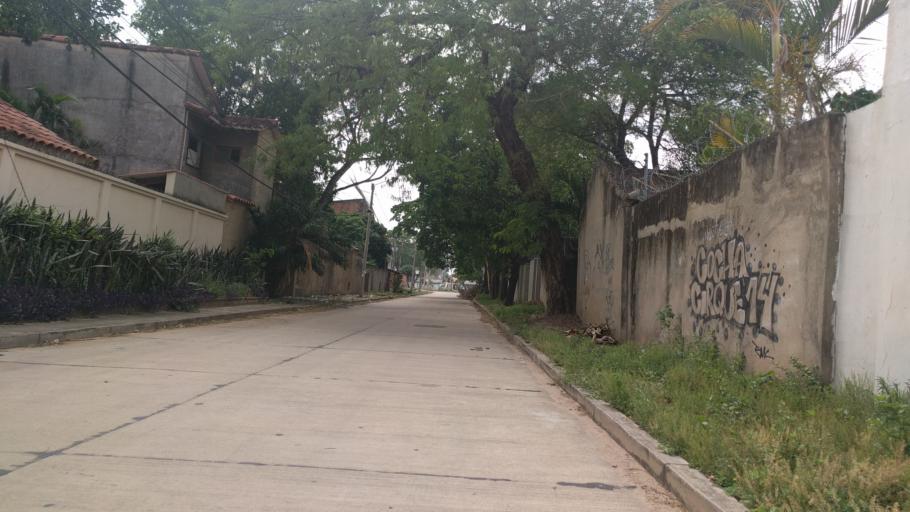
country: BO
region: Santa Cruz
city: Santa Cruz de la Sierra
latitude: -17.7869
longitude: -63.2182
